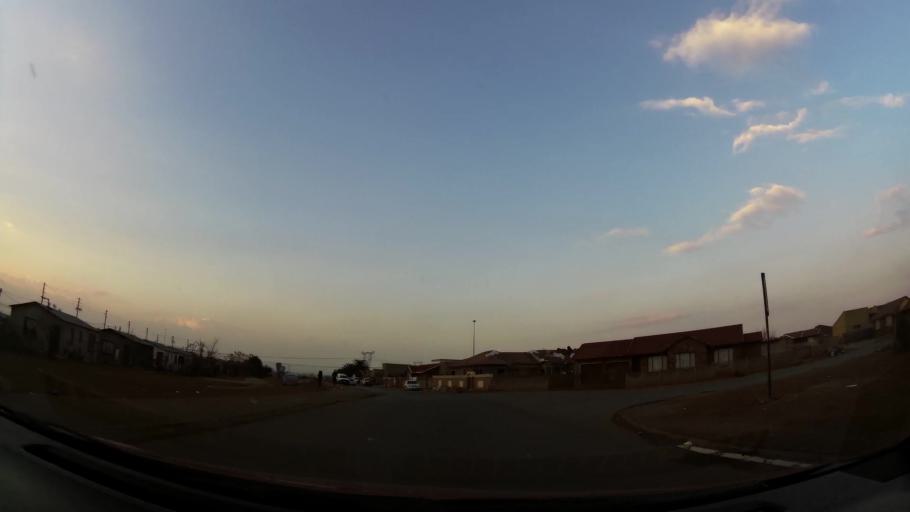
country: ZA
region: Gauteng
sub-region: City of Johannesburg Metropolitan Municipality
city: Orange Farm
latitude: -26.5610
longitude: 27.8544
